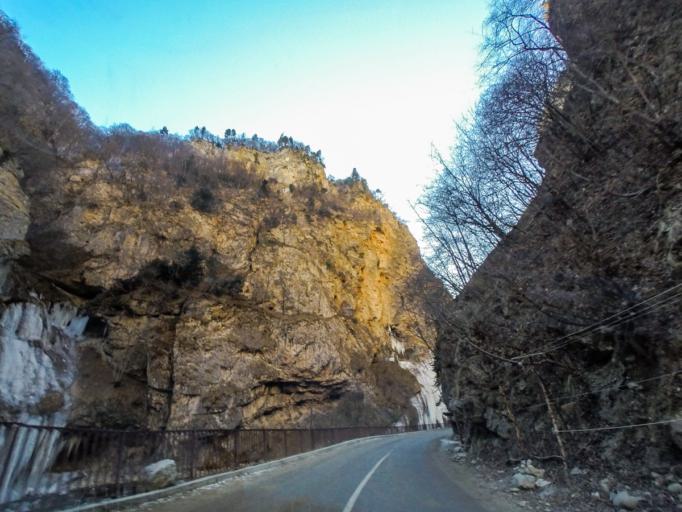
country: RU
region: Kabardino-Balkariya
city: Zhankhoteko
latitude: 43.4177
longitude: 43.2185
